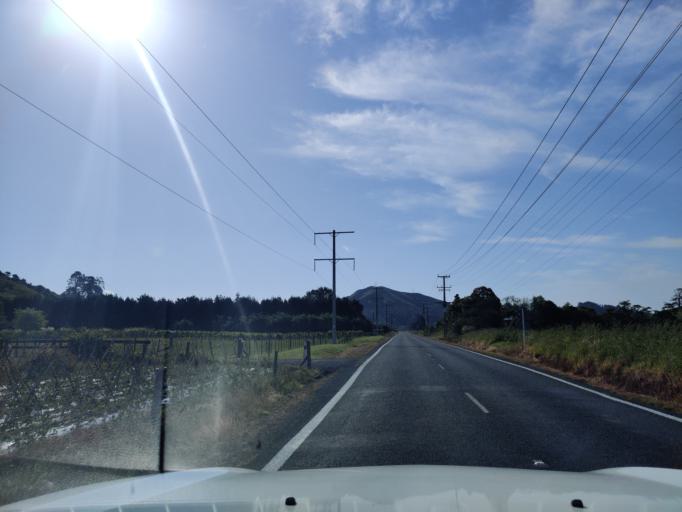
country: NZ
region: Waikato
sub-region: Waikato District
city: Ngaruawahia
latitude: -37.6063
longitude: 175.1730
